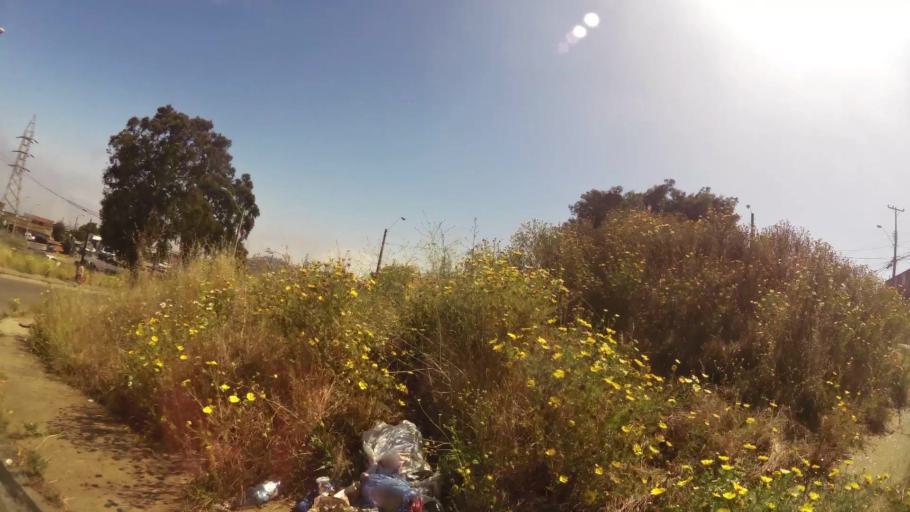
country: CL
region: Valparaiso
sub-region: Provincia de Valparaiso
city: Valparaiso
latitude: -33.0469
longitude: -71.6503
